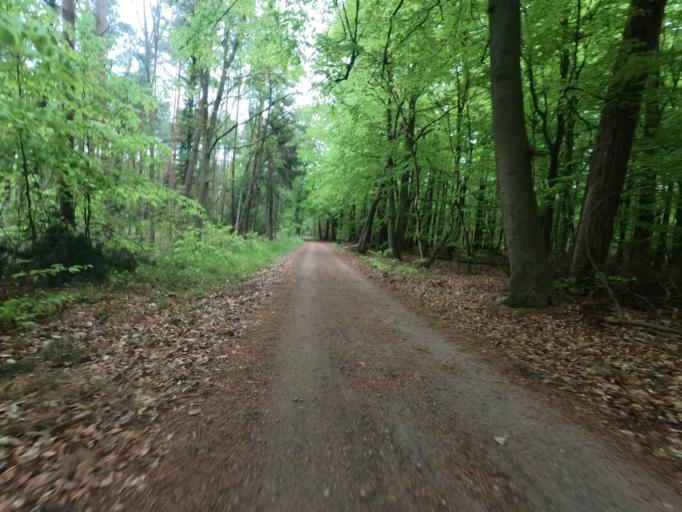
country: DE
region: Mecklenburg-Vorpommern
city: Born
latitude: 54.4041
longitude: 12.4927
